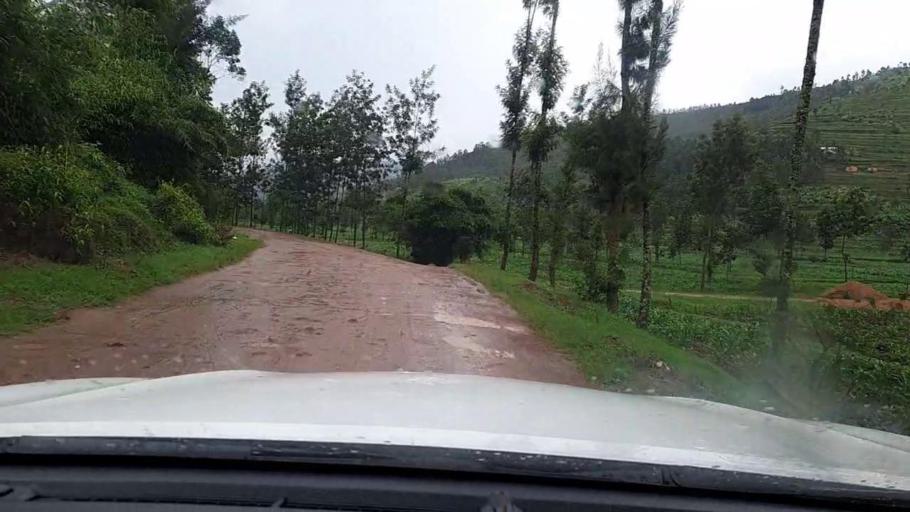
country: RW
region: Northern Province
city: Byumba
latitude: -1.7334
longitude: 29.9401
